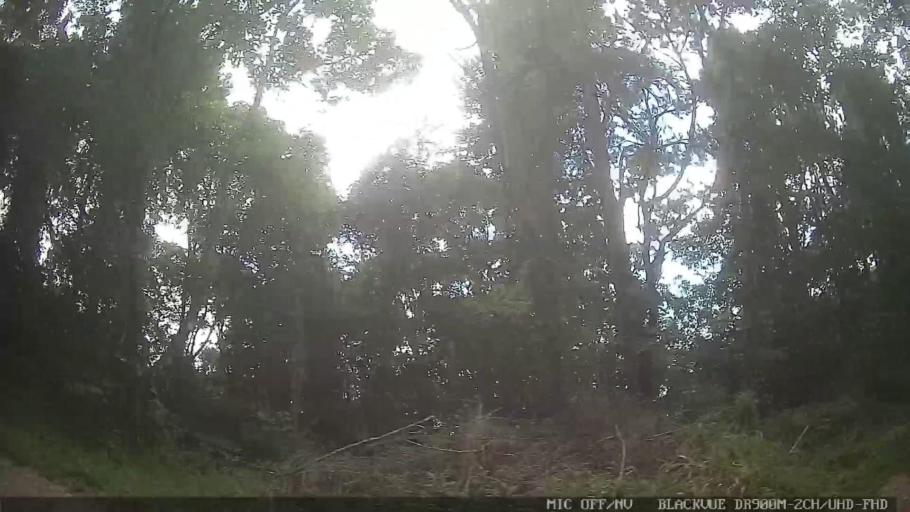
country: BR
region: Minas Gerais
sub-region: Extrema
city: Extrema
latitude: -22.8788
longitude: -46.3229
